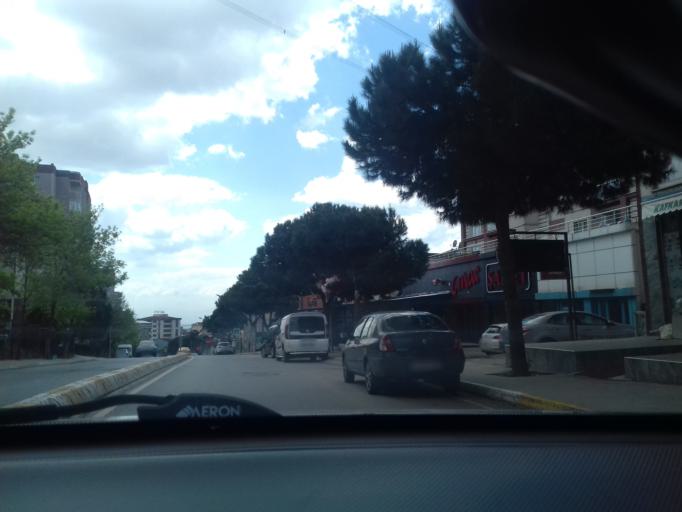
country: TR
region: Istanbul
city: Pendik
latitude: 40.9130
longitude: 29.2827
